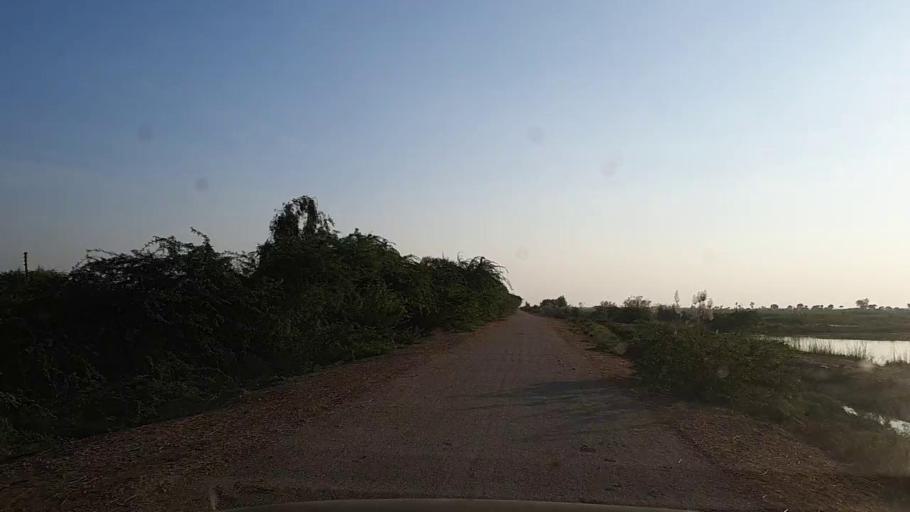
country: PK
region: Sindh
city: Thatta
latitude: 24.6203
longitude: 67.9132
